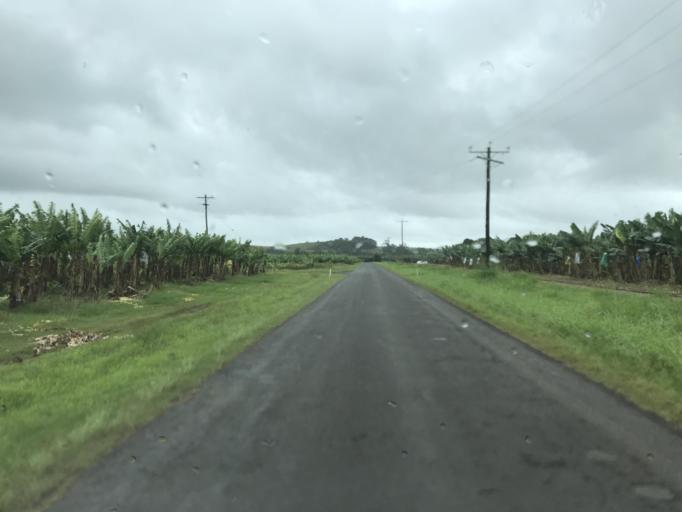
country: AU
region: Queensland
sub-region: Cassowary Coast
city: Innisfail
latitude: -17.5088
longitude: 145.9789
